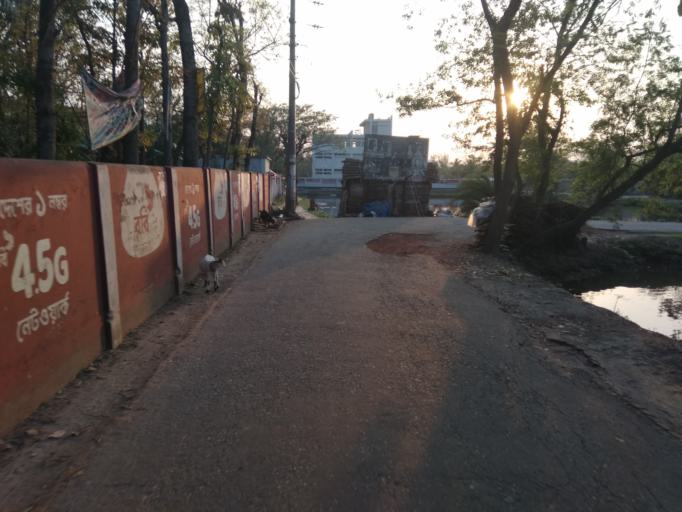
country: BD
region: Khulna
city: Satkhira
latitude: 22.5461
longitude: 89.1730
